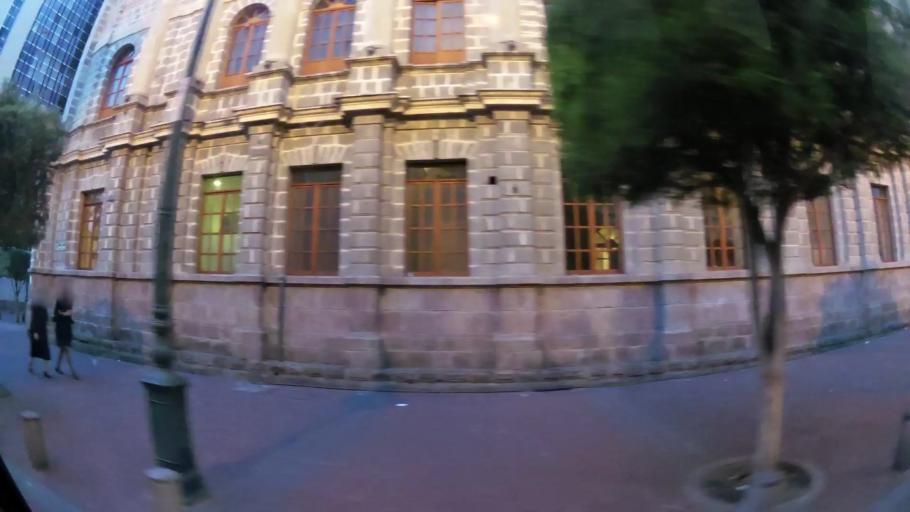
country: EC
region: Tungurahua
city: Ambato
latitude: -1.2429
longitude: -78.6294
